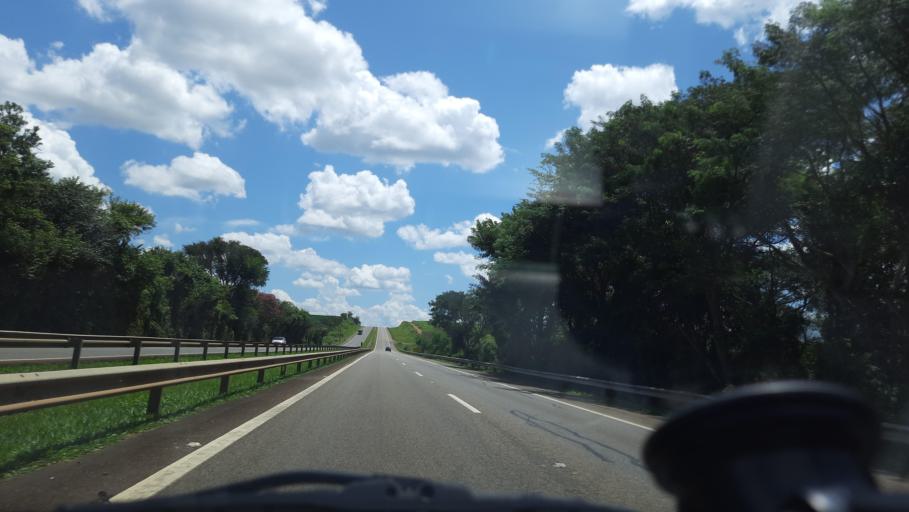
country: BR
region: Sao Paulo
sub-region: Aguai
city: Aguai
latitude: -21.9897
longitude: -47.0395
